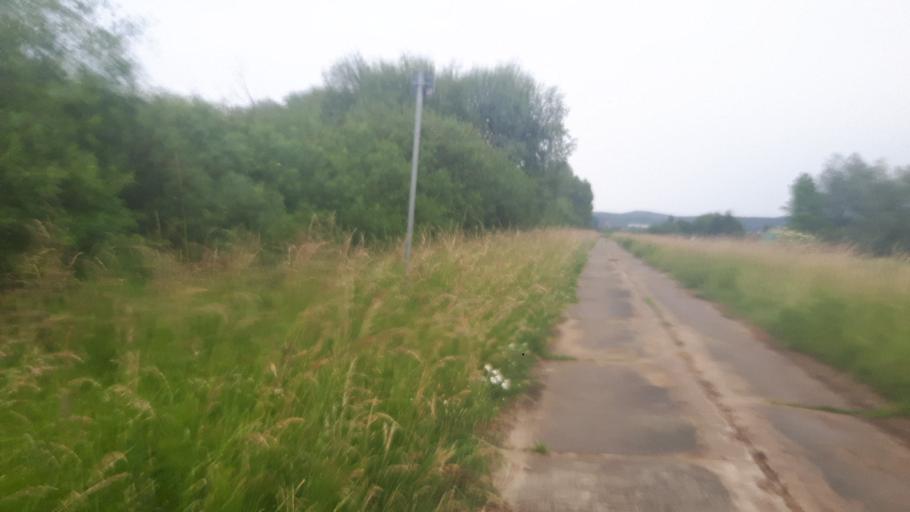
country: PL
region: Warmian-Masurian Voivodeship
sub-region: Powiat elblaski
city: Tolkmicko
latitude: 54.3209
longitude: 19.5012
